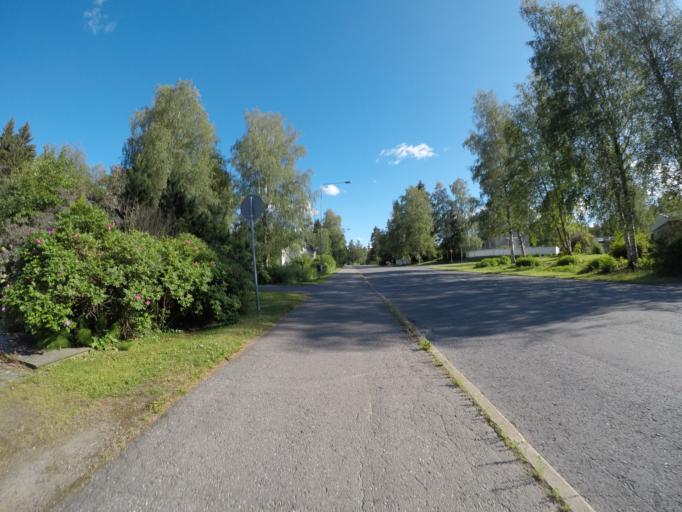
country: FI
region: Haeme
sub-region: Haemeenlinna
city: Haemeenlinna
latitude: 61.0151
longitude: 24.4982
